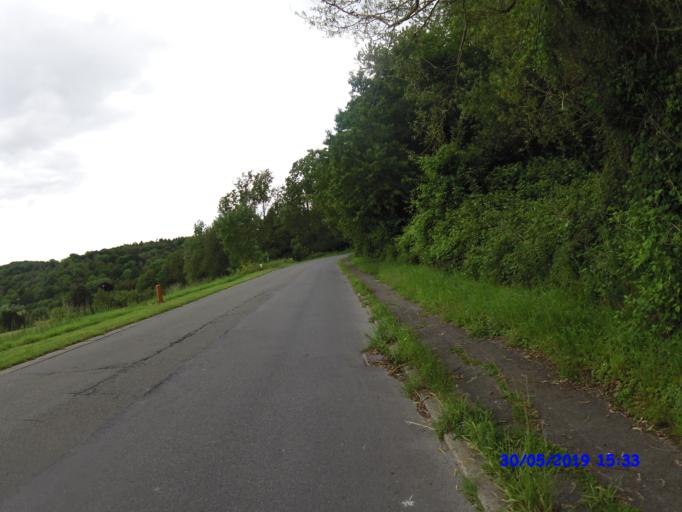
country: BE
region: Wallonia
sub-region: Province du Hainaut
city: Courcelles
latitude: 50.4032
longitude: 4.3733
